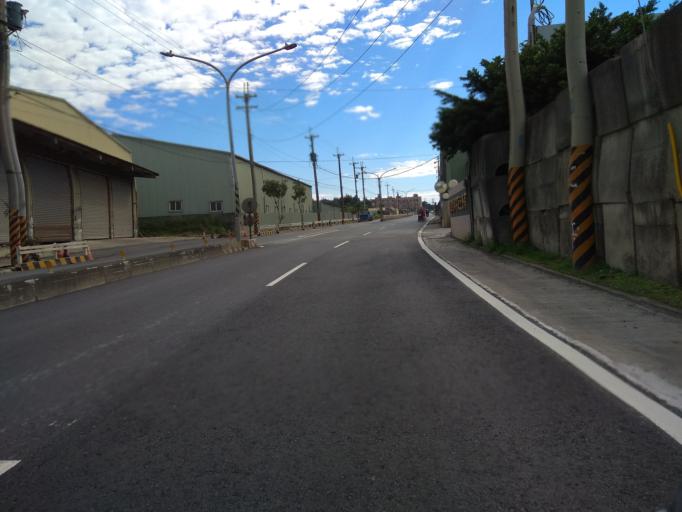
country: TW
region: Taiwan
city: Taoyuan City
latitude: 25.0617
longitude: 121.1337
